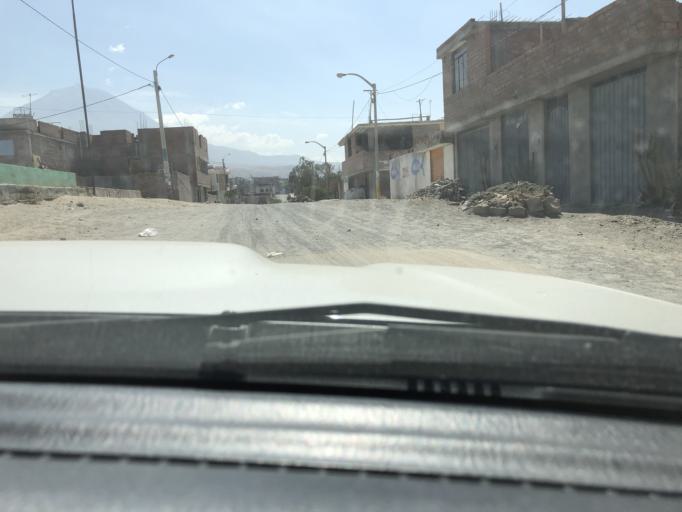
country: PE
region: Arequipa
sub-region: Provincia de Arequipa
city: Arequipa
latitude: -16.3432
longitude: -71.5520
